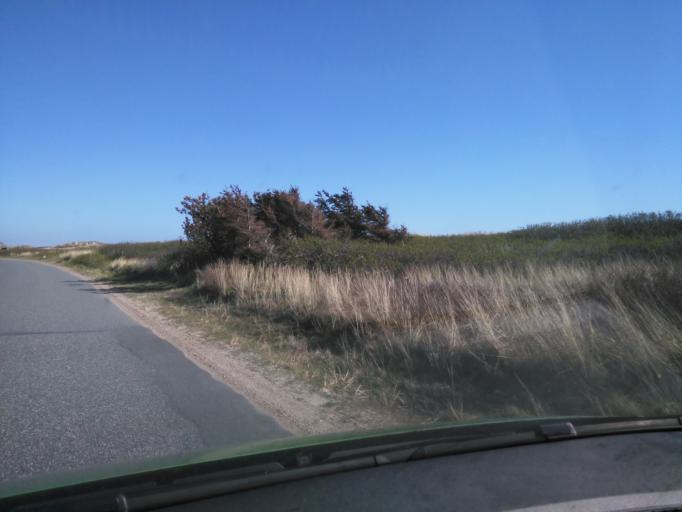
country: DK
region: South Denmark
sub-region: Varde Kommune
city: Oksbol
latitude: 55.5534
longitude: 8.0956
